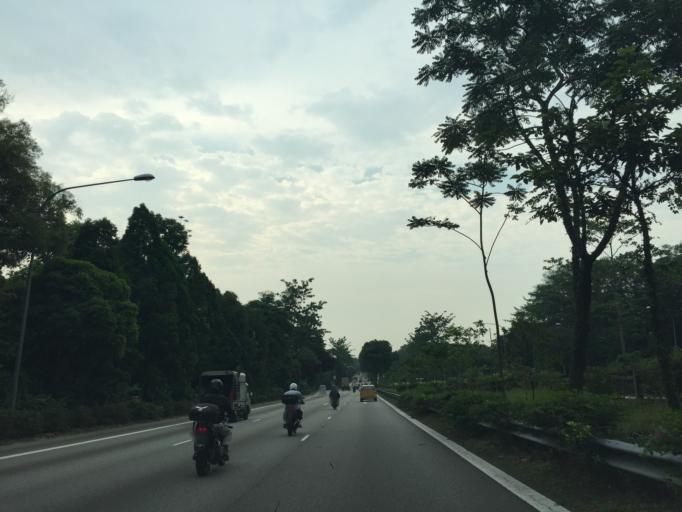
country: MY
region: Johor
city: Johor Bahru
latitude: 1.3720
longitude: 103.7781
